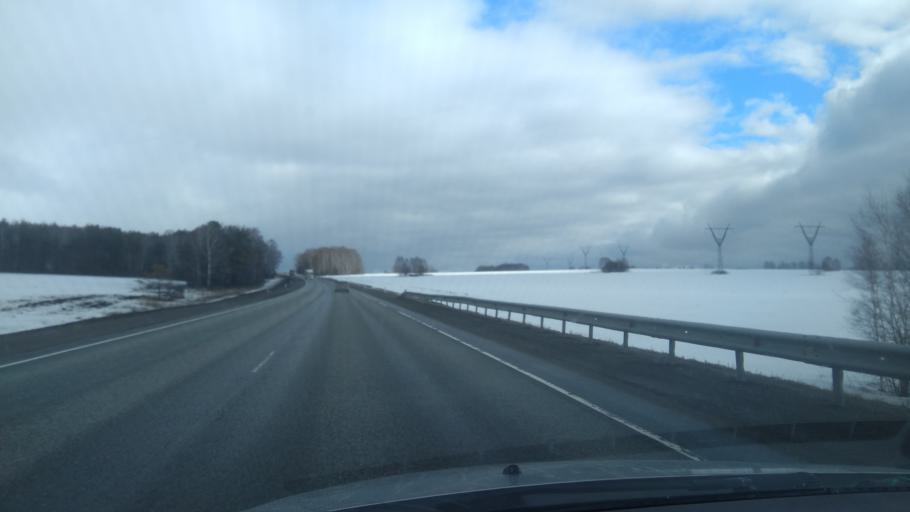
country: RU
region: Sverdlovsk
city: Ufimskiy
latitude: 56.7720
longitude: 58.0280
